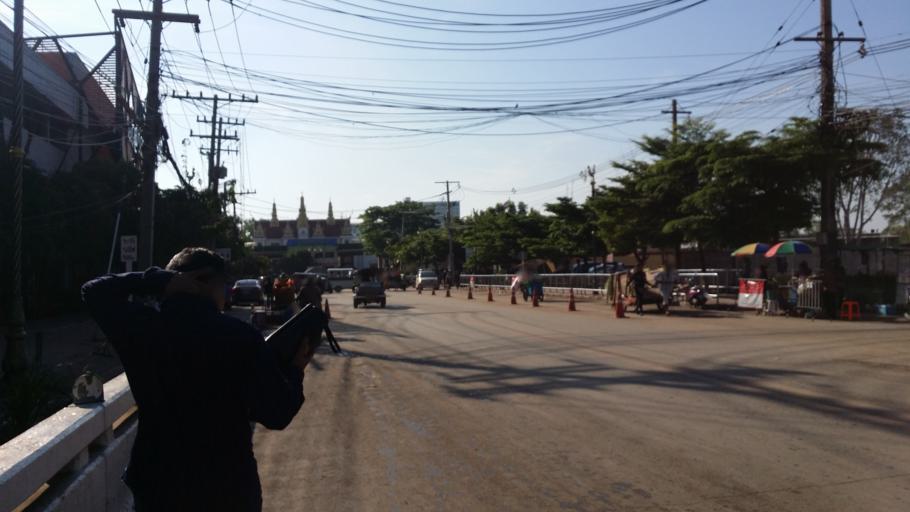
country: KH
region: Banteay Meanchey
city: Paoy Pet
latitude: 13.6633
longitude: 102.5468
